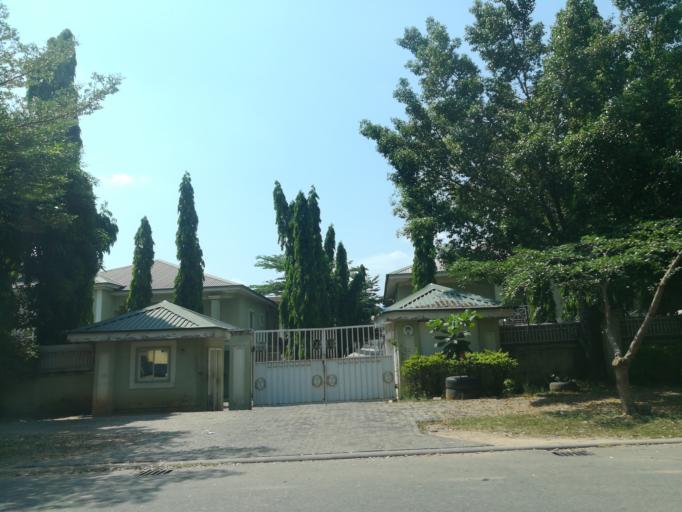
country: NG
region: Abuja Federal Capital Territory
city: Abuja
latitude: 9.0693
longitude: 7.4271
